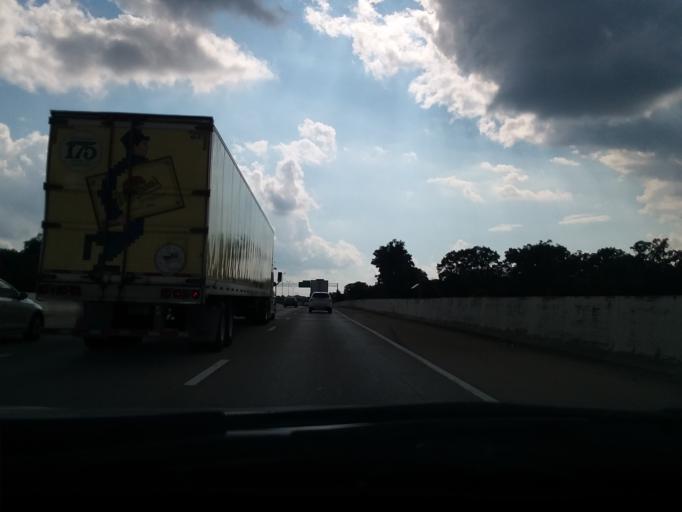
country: US
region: Tennessee
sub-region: Davidson County
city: Lakewood
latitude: 36.2358
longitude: -86.7123
